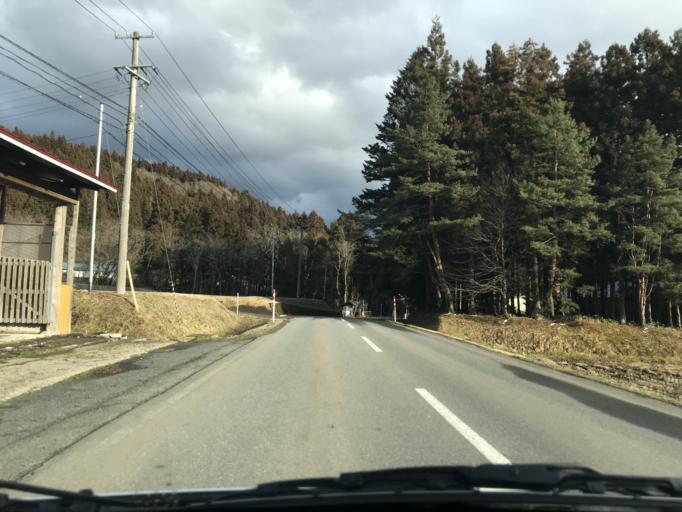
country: JP
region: Iwate
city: Mizusawa
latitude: 39.0618
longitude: 141.0337
